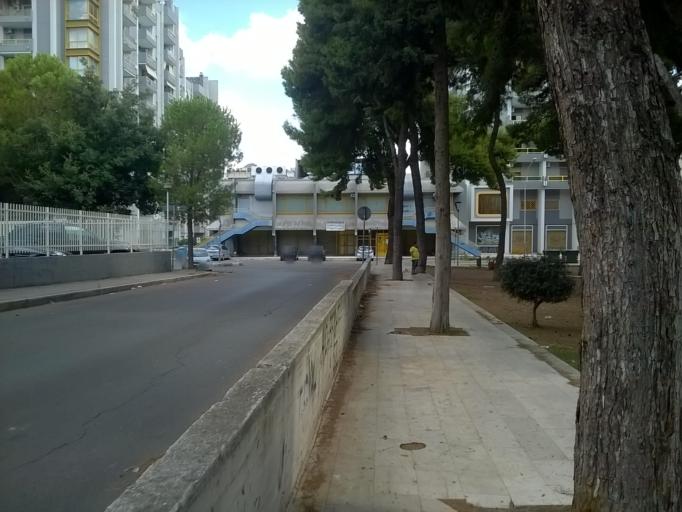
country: IT
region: Apulia
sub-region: Provincia di Taranto
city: Taranto
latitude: 40.4600
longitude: 17.2708
